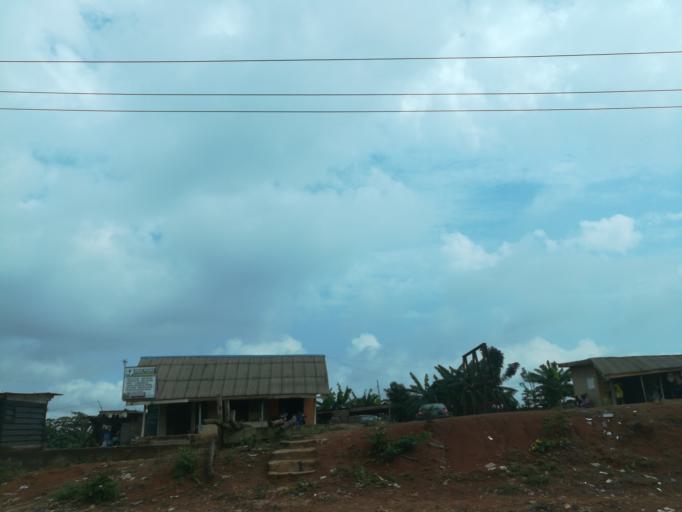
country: NG
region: Lagos
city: Ikorodu
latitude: 6.6618
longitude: 3.5929
